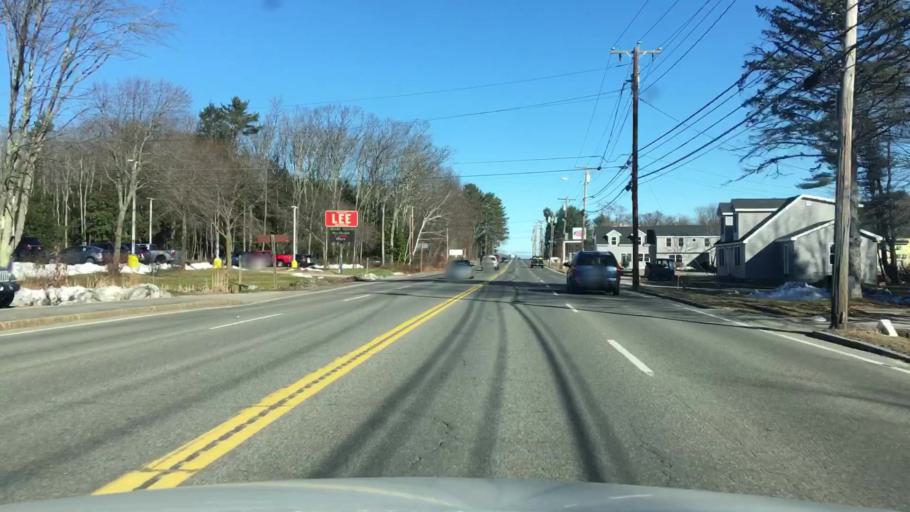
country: US
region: Maine
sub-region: York County
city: Saco
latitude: 43.5346
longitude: -70.4239
